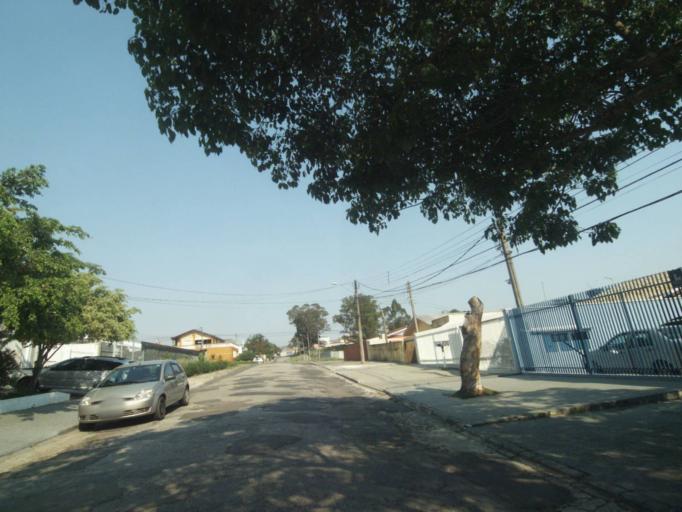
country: BR
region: Parana
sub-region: Curitiba
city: Curitiba
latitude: -25.5007
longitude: -49.2768
